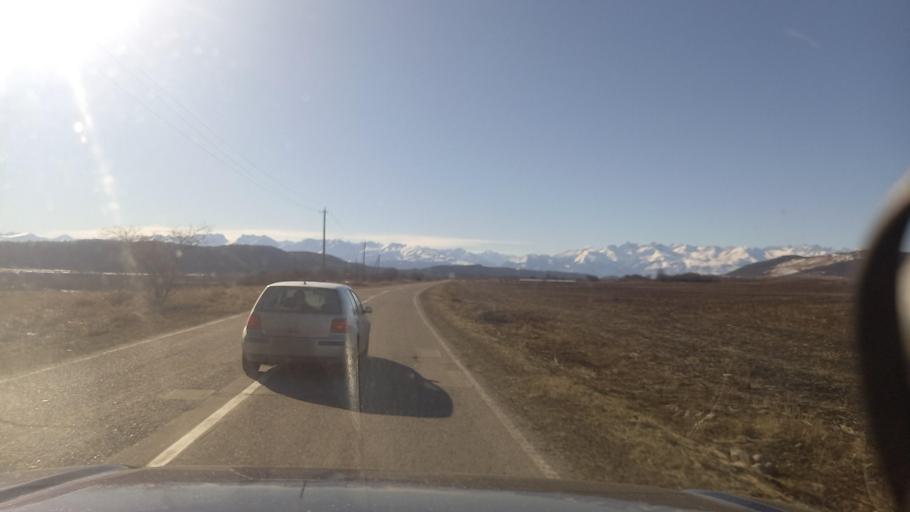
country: RU
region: Kabardino-Balkariya
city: Urukh
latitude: 43.2907
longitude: 44.0098
